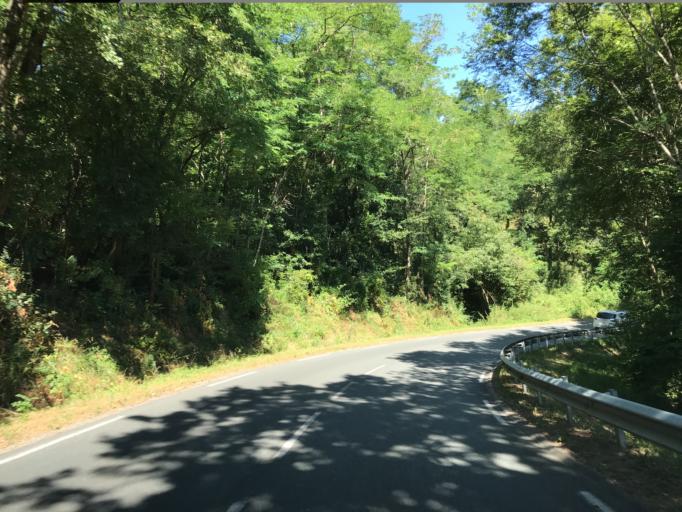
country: FR
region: Limousin
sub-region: Departement de la Correze
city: Larche
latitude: 45.1047
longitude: 1.3848
